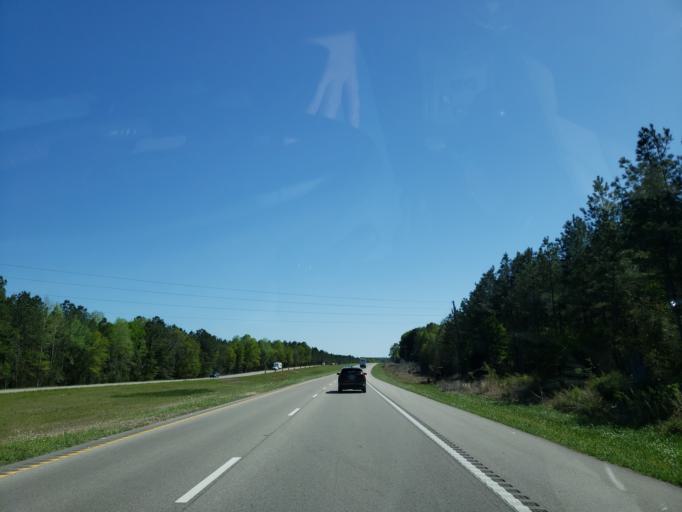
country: US
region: Mississippi
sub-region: Stone County
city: Wiggins
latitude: 31.0052
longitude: -89.2019
